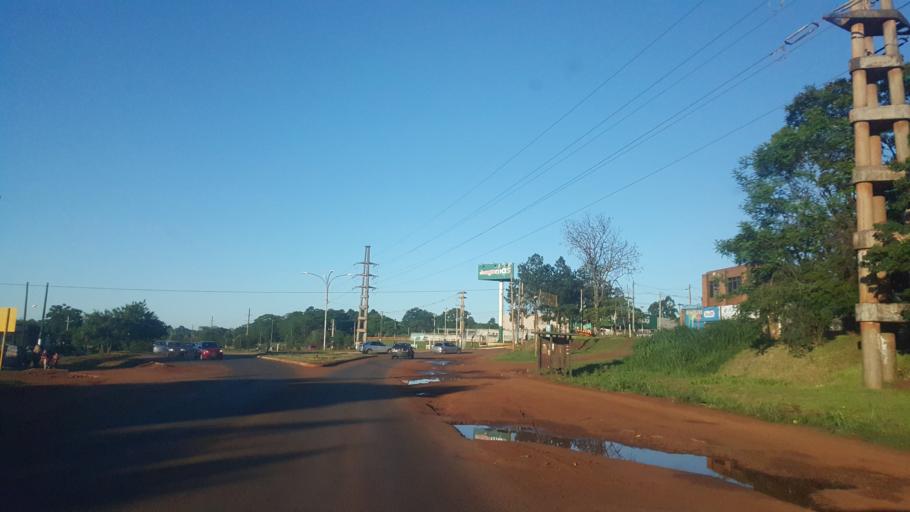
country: AR
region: Misiones
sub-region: Departamento de Capital
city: Posadas
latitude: -27.4262
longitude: -55.9349
